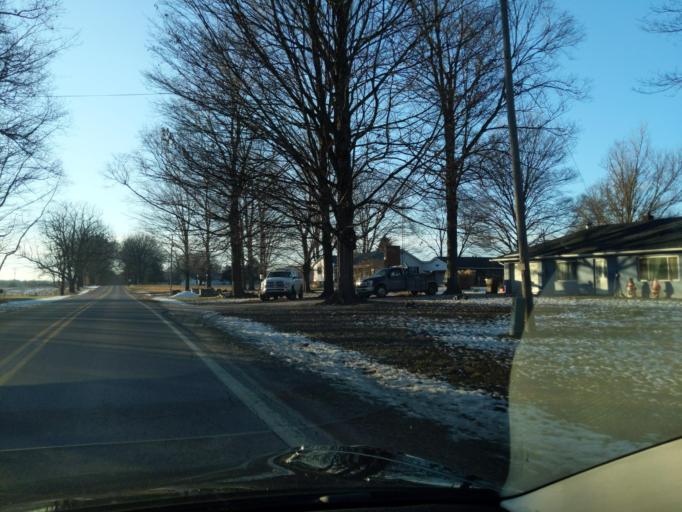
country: US
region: Michigan
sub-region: Ingham County
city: Stockbridge
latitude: 42.4679
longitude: -84.0937
